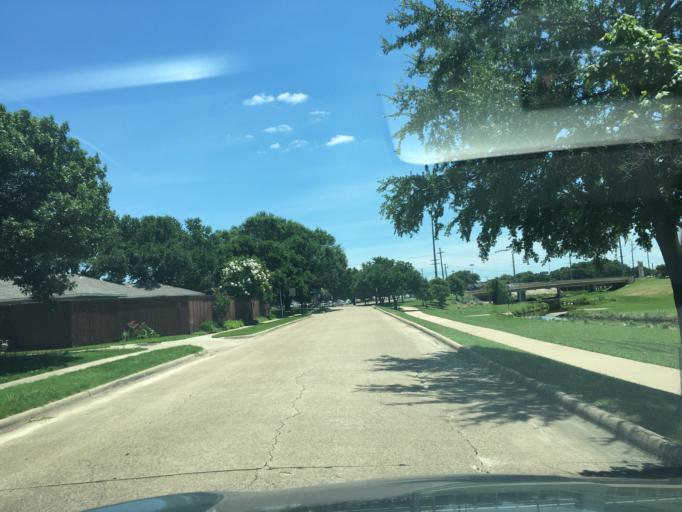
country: US
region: Texas
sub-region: Dallas County
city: Richardson
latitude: 32.9485
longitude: -96.6844
